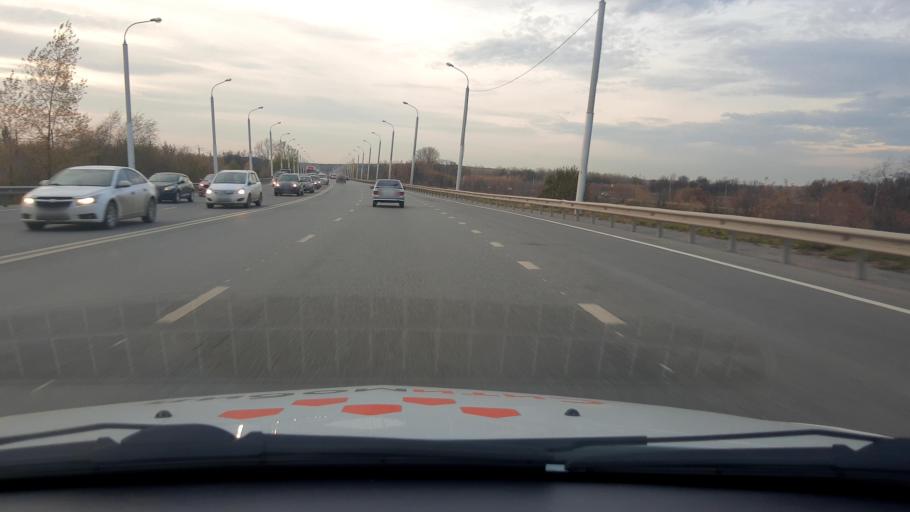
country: RU
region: Bashkortostan
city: Iglino
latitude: 54.7993
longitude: 56.2018
